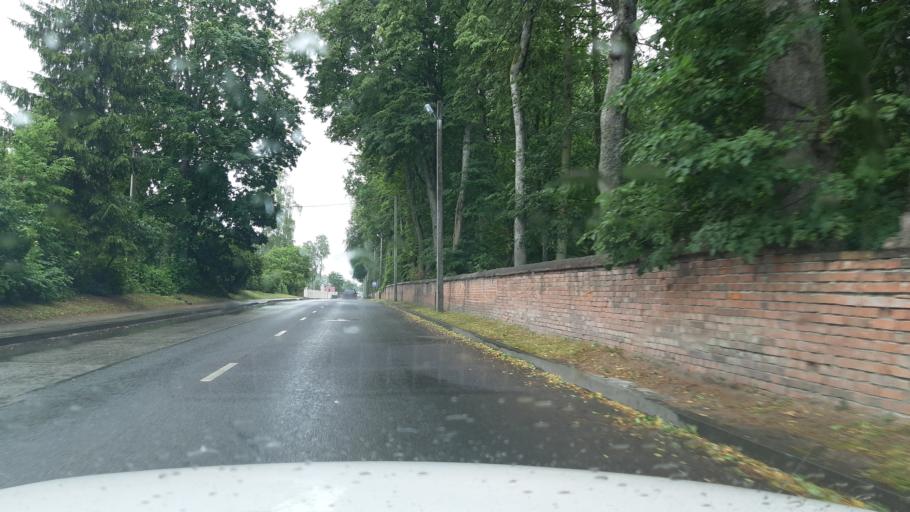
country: LT
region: Taurages apskritis
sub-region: Jurbarkas
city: Jurbarkas
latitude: 55.0825
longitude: 22.7498
